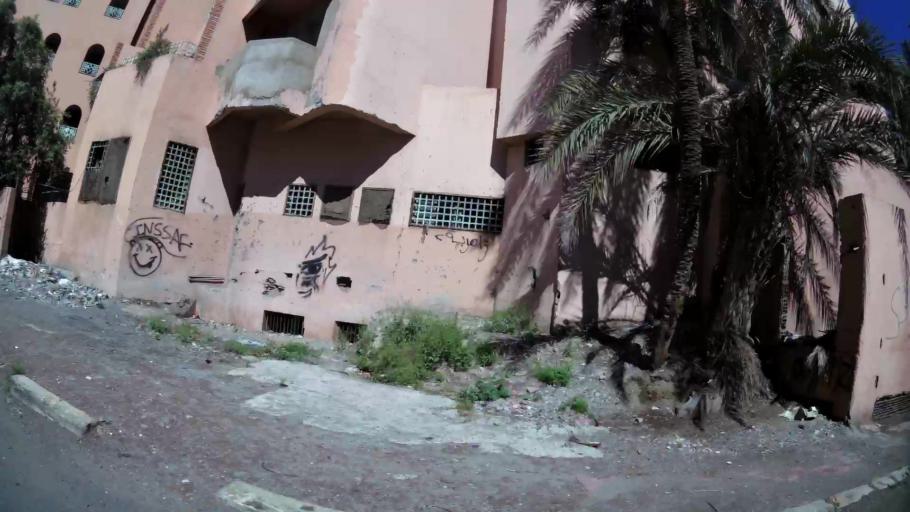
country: MA
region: Marrakech-Tensift-Al Haouz
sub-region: Marrakech
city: Marrakesh
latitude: 31.6379
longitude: -8.0074
